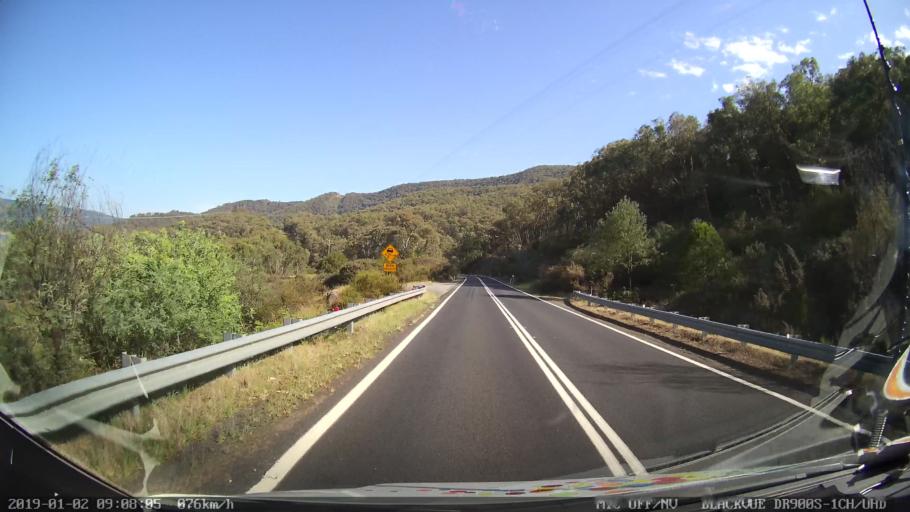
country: AU
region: New South Wales
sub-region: Tumut Shire
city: Tumut
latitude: -35.5338
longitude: 148.2947
